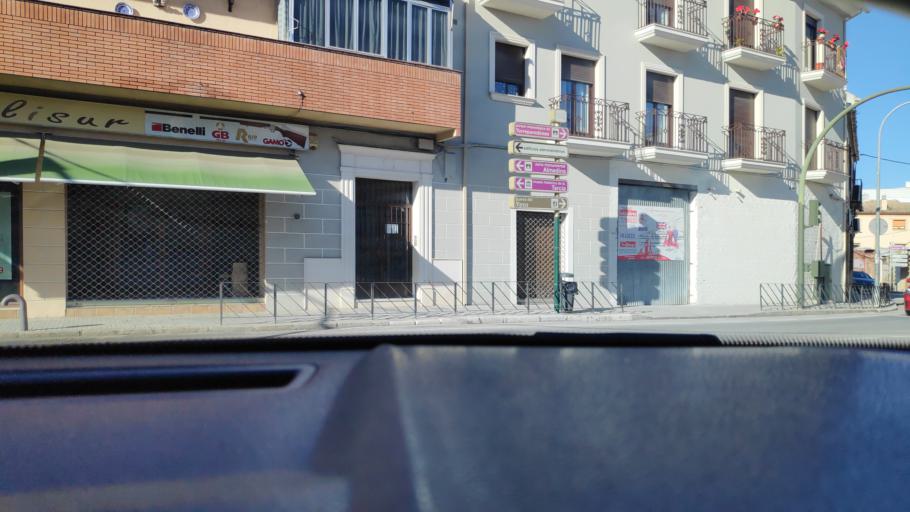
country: ES
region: Andalusia
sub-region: Province of Cordoba
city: Baena
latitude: 37.6165
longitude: -4.3235
